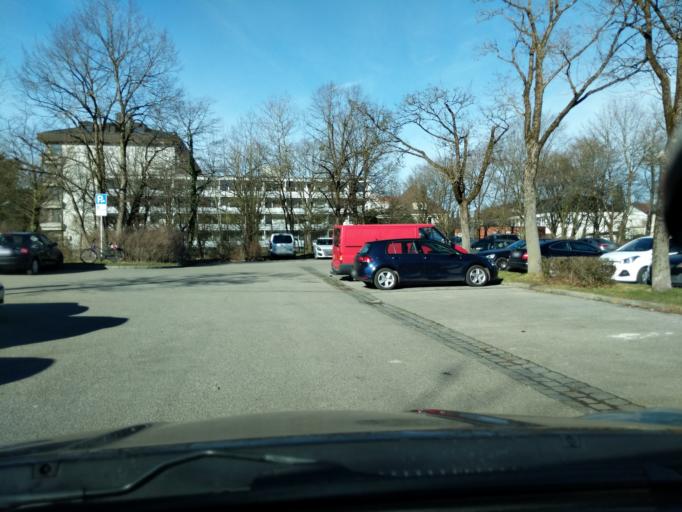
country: DE
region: Bavaria
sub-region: Upper Bavaria
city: Neuried
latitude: 48.1071
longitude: 11.5029
